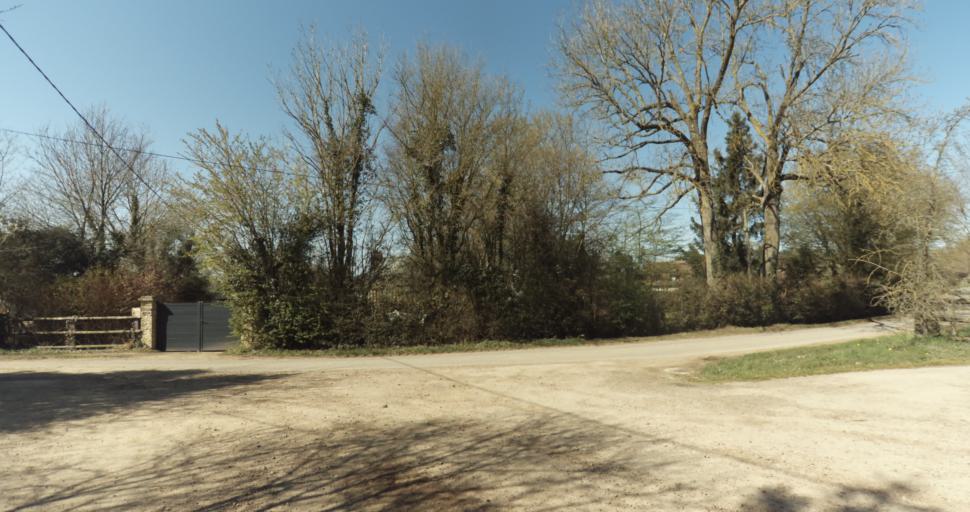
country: FR
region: Lower Normandy
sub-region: Departement du Calvados
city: Livarot
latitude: 49.0194
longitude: 0.1046
